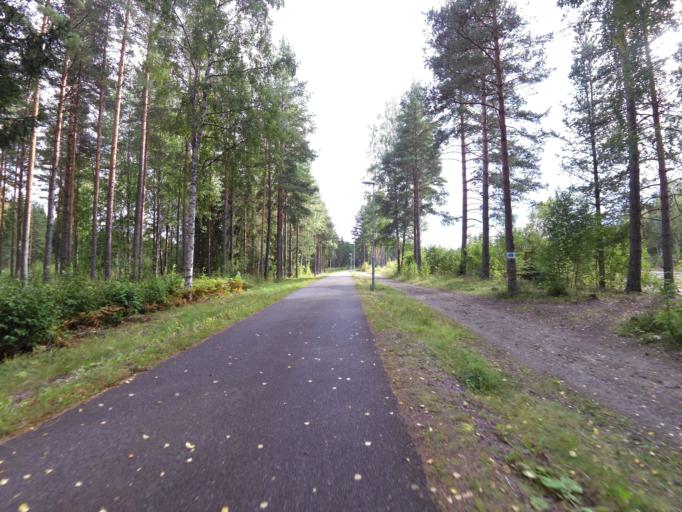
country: SE
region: Gaevleborg
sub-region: Sandvikens Kommun
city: Sandviken
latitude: 60.6811
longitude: 16.8166
